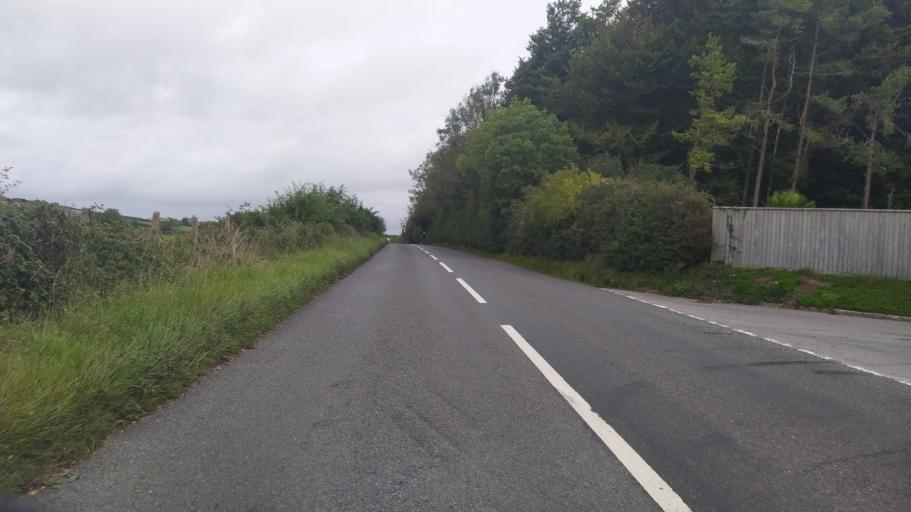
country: GB
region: England
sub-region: Dorset
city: Dorchester
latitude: 50.7676
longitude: -2.3970
